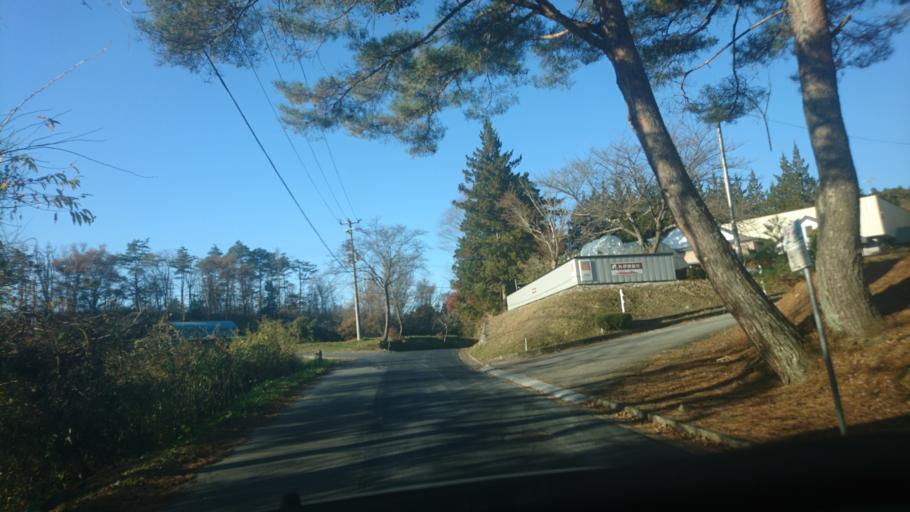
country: JP
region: Iwate
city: Ichinoseki
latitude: 38.8978
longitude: 141.2336
